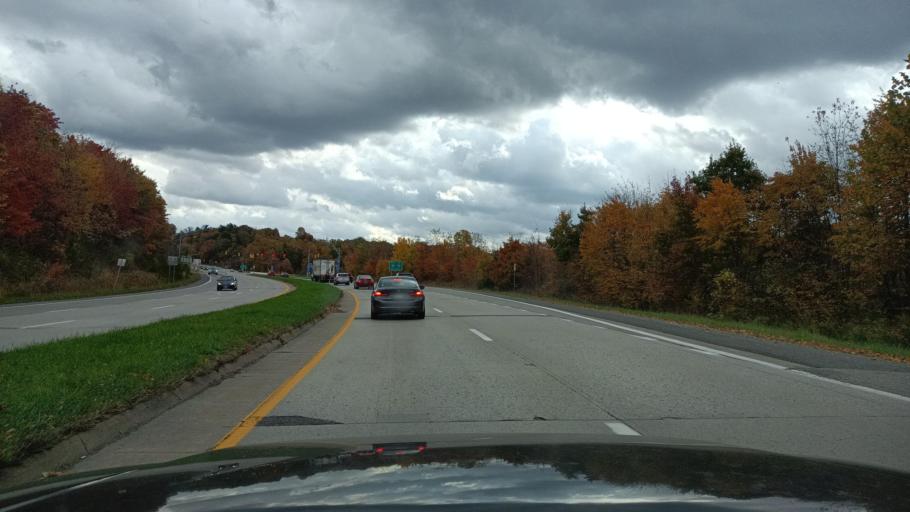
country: US
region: West Virginia
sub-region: Monongalia County
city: Brookhaven
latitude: 39.6471
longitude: -79.8989
